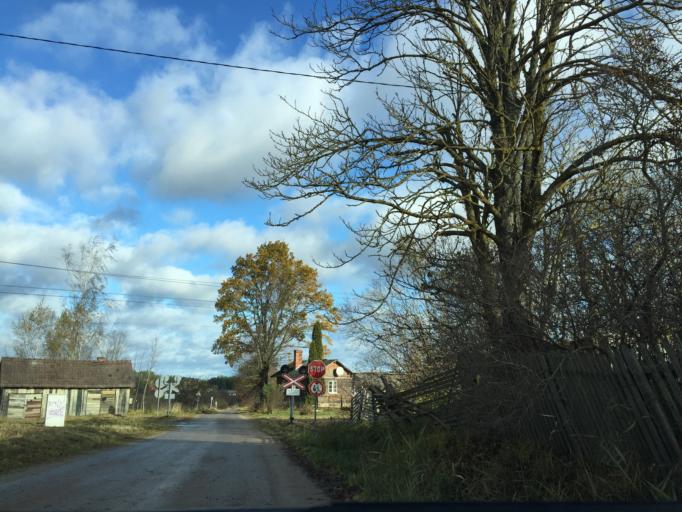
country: LV
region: Tukuma Rajons
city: Tukums
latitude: 56.9697
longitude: 23.2281
